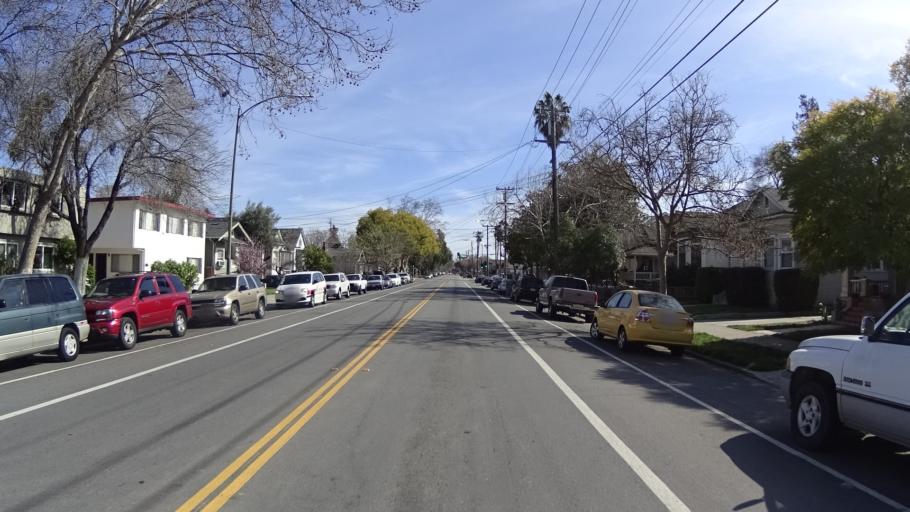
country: US
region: California
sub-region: Santa Clara County
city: San Jose
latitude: 37.3447
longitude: -121.8883
